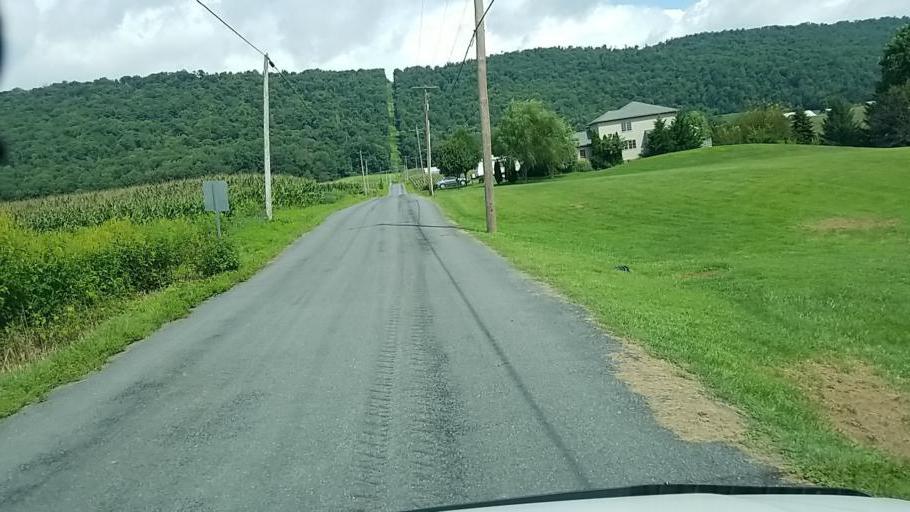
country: US
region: Pennsylvania
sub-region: Dauphin County
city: Millersburg
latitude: 40.5759
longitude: -76.9318
